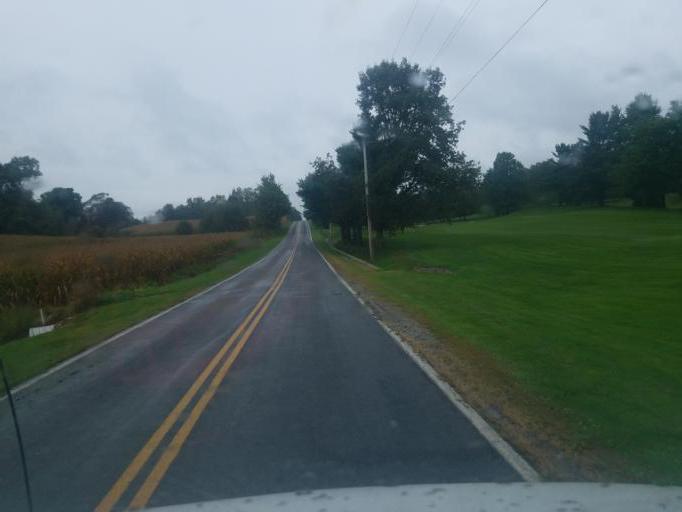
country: US
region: Ohio
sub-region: Wayne County
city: Rittman
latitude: 40.9928
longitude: -81.8154
